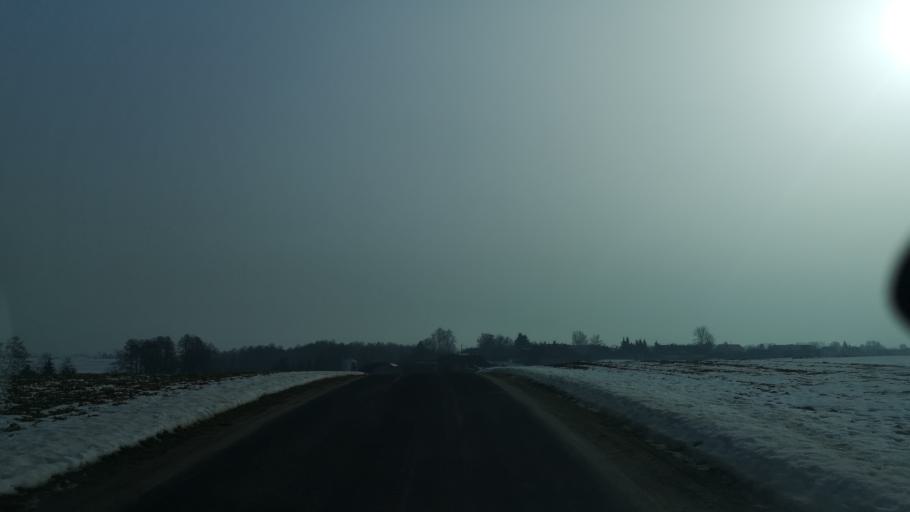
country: PL
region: Warmian-Masurian Voivodeship
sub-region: Powiat nowomiejski
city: Biskupiec
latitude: 53.5319
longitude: 19.3532
